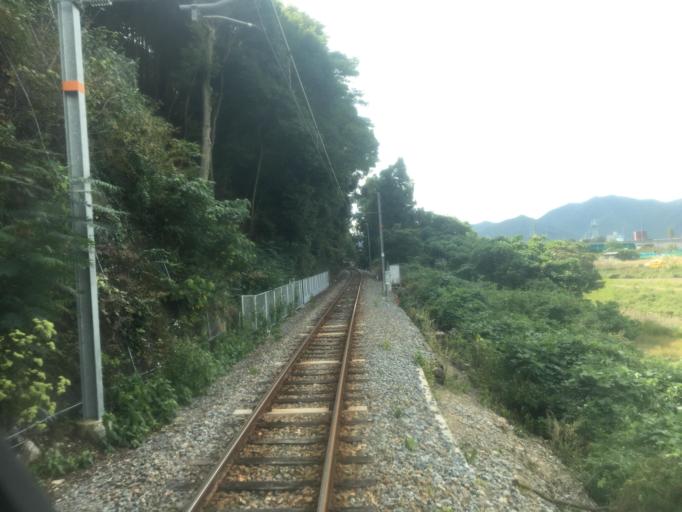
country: JP
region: Hyogo
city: Nishiwaki
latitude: 34.9800
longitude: 134.9868
